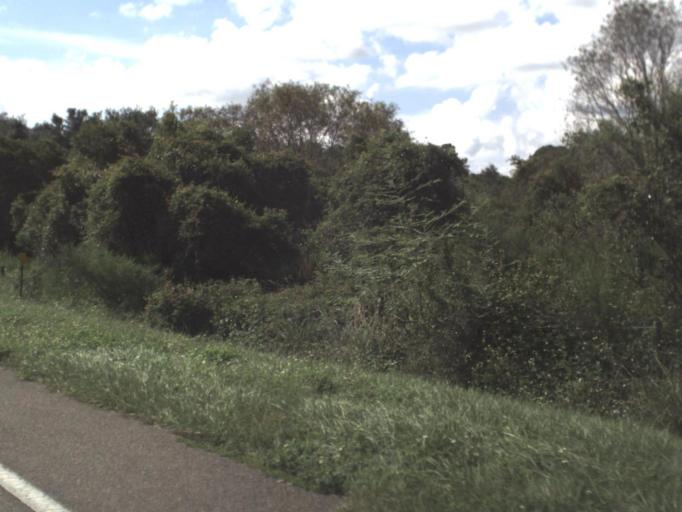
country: US
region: Florida
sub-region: Hardee County
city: Wauchula
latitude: 27.4855
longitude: -81.9481
